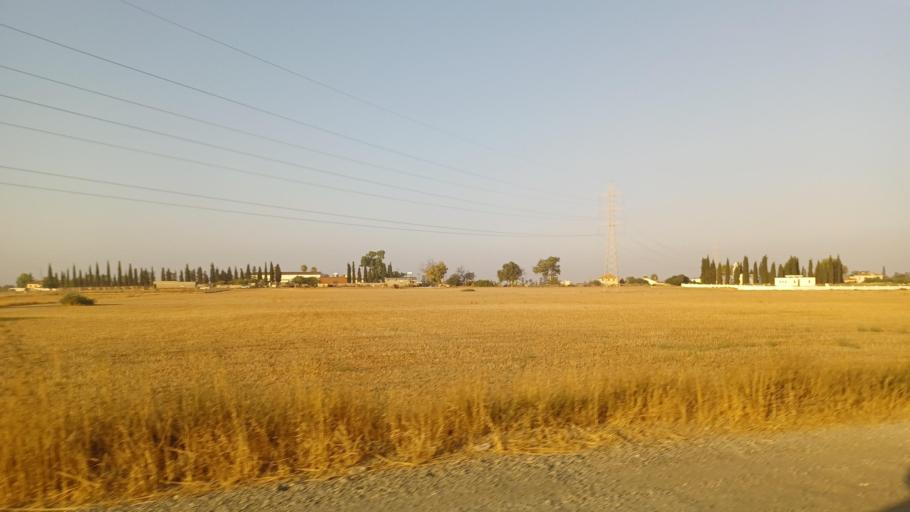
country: CY
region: Ammochostos
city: Avgorou
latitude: 35.0332
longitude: 33.8526
